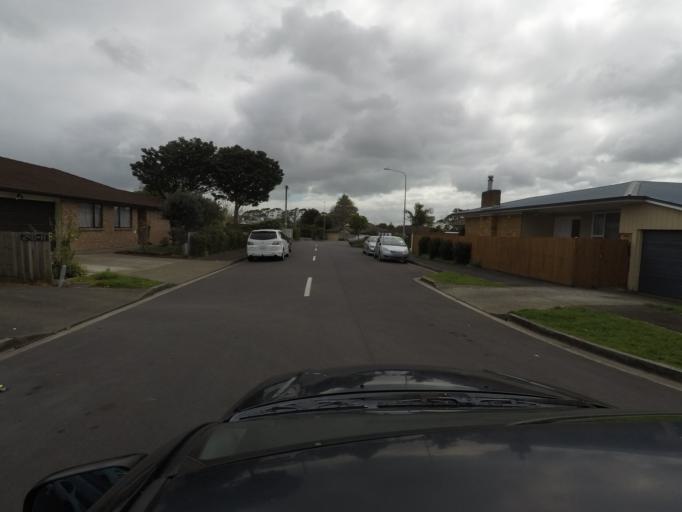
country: NZ
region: Auckland
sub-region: Auckland
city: Tamaki
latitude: -36.9327
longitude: 174.8548
